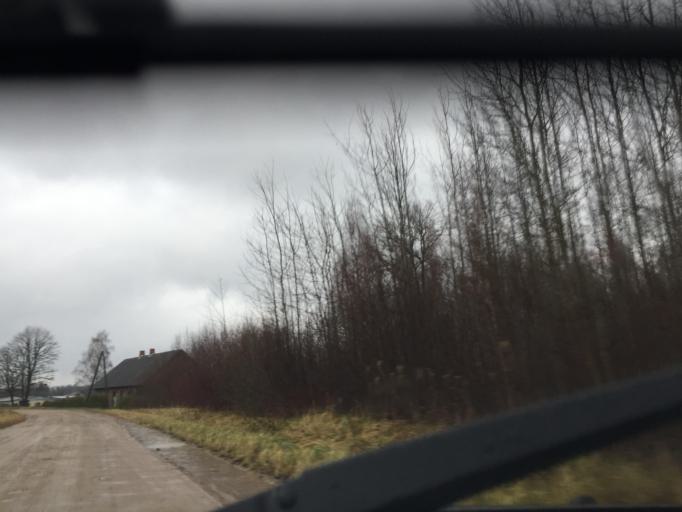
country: LV
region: Limbazu Rajons
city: Limbazi
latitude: 57.6512
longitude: 24.7771
